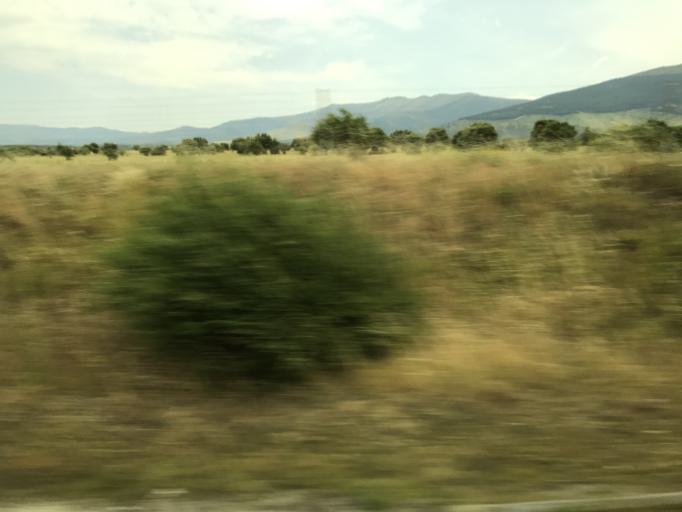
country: ES
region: Castille and Leon
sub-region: Provincia de Segovia
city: Cerezo de Abajo
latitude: 41.2014
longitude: -3.5812
